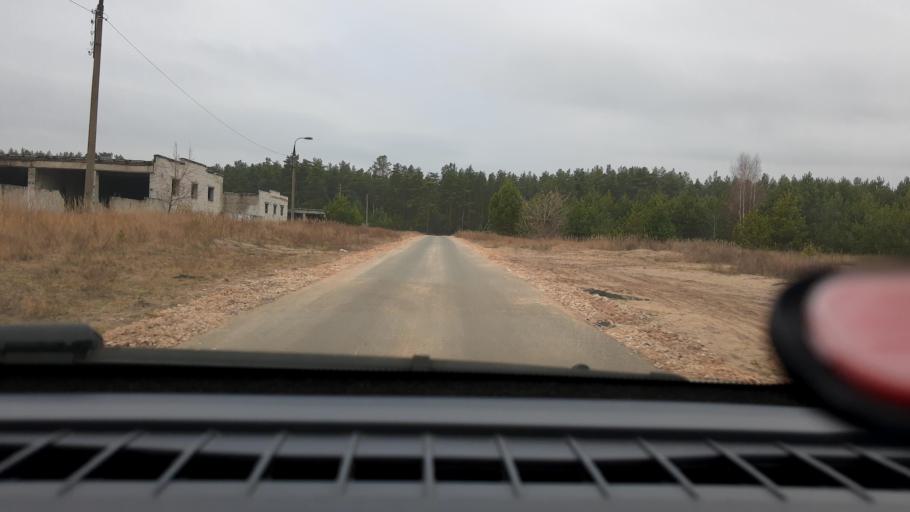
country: RU
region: Nizjnij Novgorod
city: Lukino
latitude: 56.3926
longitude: 43.7170
